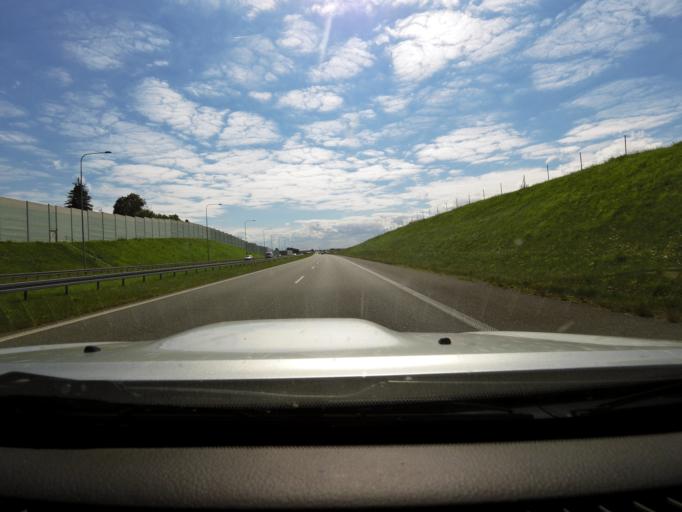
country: PL
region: Warmian-Masurian Voivodeship
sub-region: Powiat ostrodzki
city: Milomlyn
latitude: 53.8120
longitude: 19.7827
